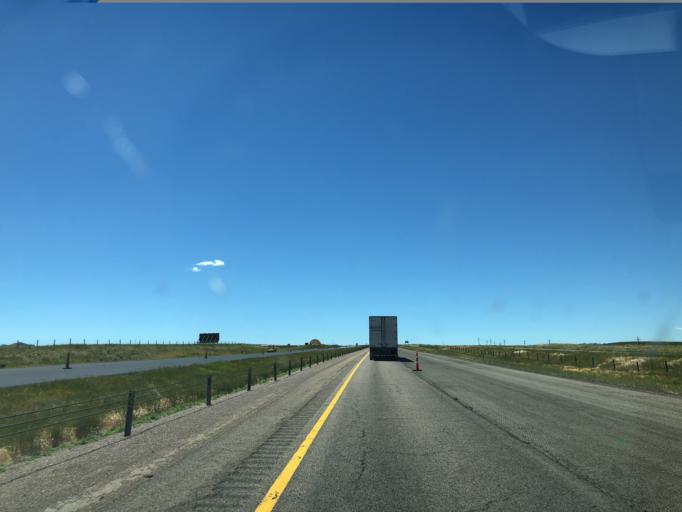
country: US
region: Wyoming
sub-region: Laramie County
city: Cheyenne
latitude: 41.0990
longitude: -105.1395
